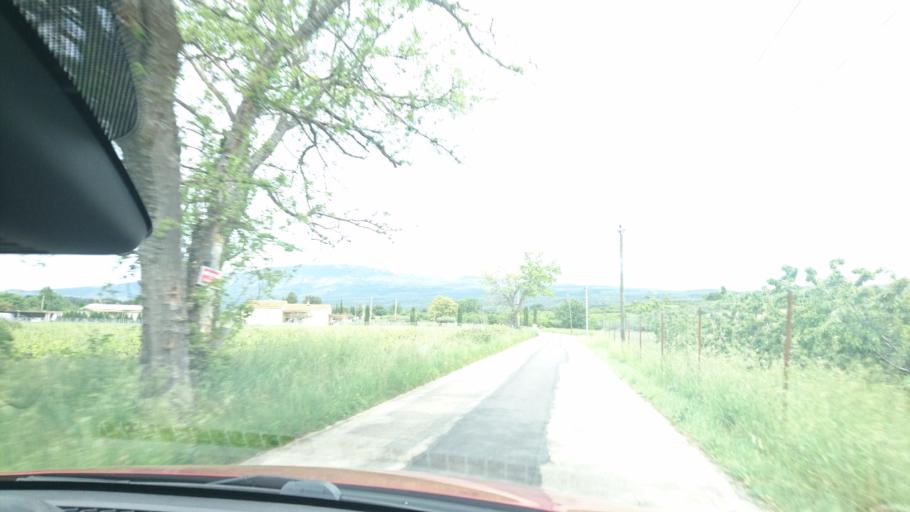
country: FR
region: Provence-Alpes-Cote d'Azur
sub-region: Departement du Vaucluse
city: Villes-sur-Auzon
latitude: 44.0712
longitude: 5.2332
